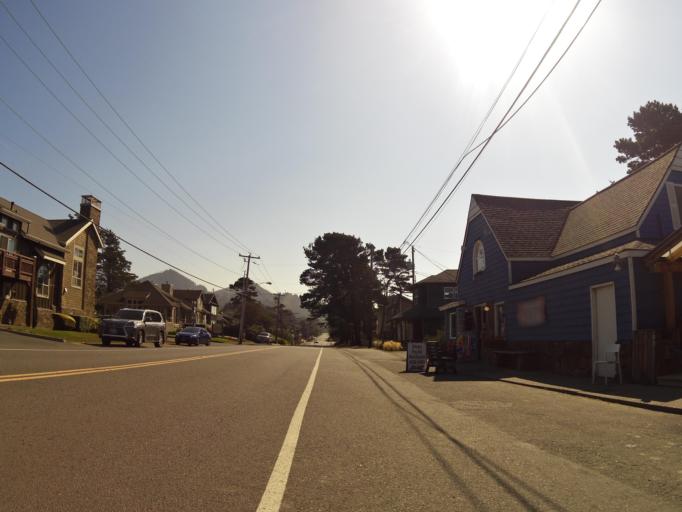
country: US
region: Oregon
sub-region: Clatsop County
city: Cannon Beach
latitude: 45.8745
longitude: -123.9599
